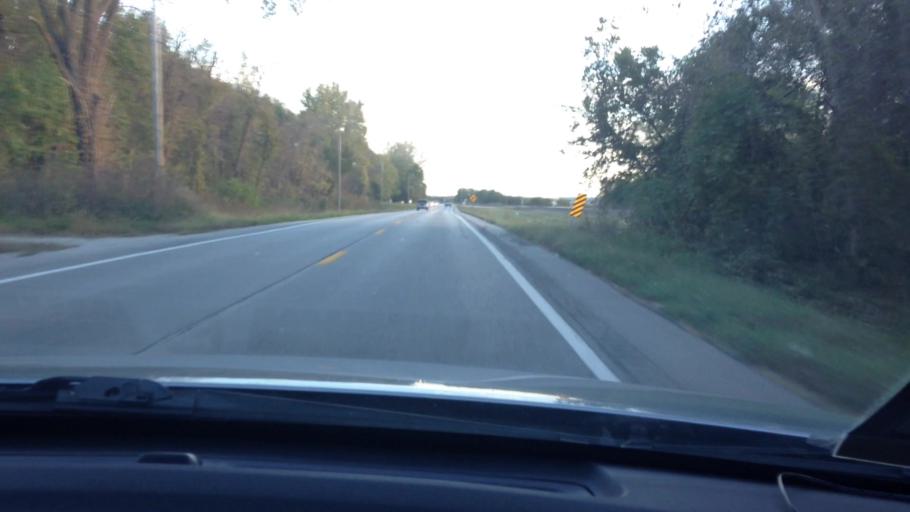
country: US
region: Kansas
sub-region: Leavenworth County
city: Leavenworth
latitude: 39.3063
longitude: -94.8487
